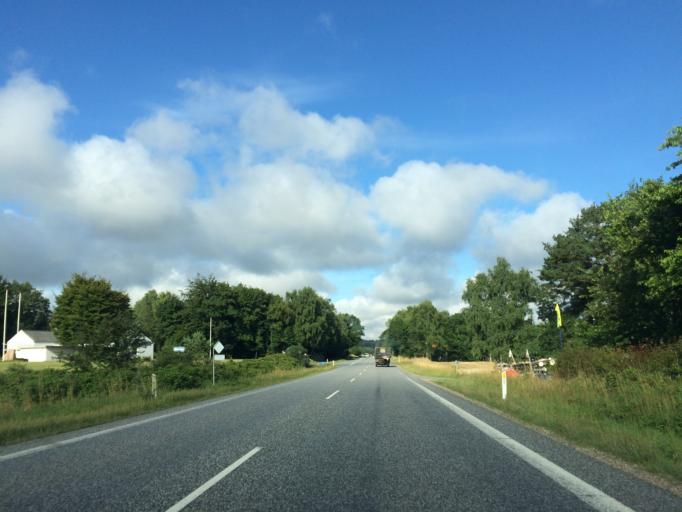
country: DK
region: Central Jutland
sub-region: Viborg Kommune
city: Bjerringbro
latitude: 56.3036
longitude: 9.6362
